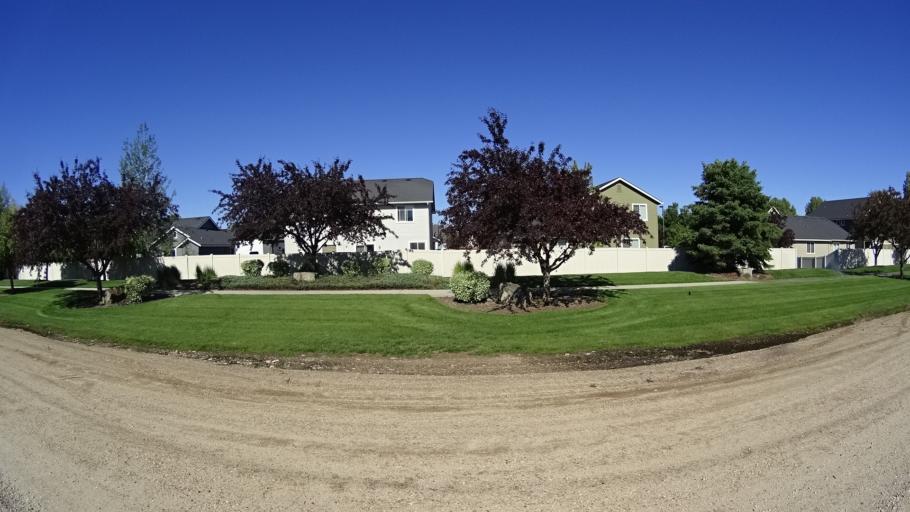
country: US
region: Idaho
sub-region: Ada County
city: Meridian
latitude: 43.6365
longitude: -116.4536
